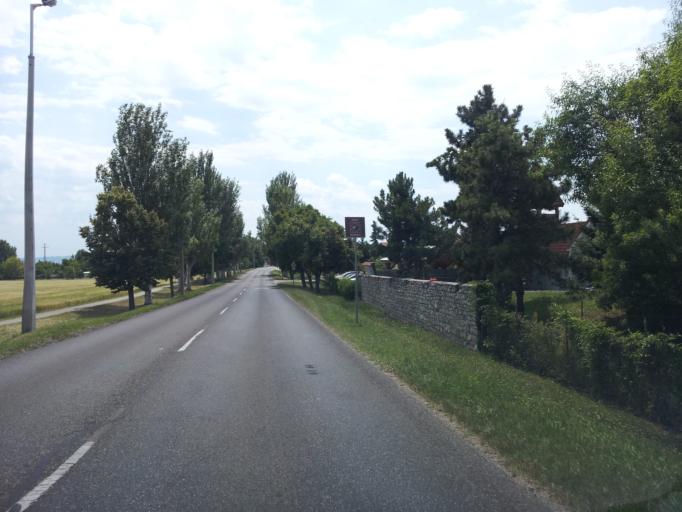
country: HU
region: Veszprem
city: Balatonfured
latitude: 46.9159
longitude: 17.8181
